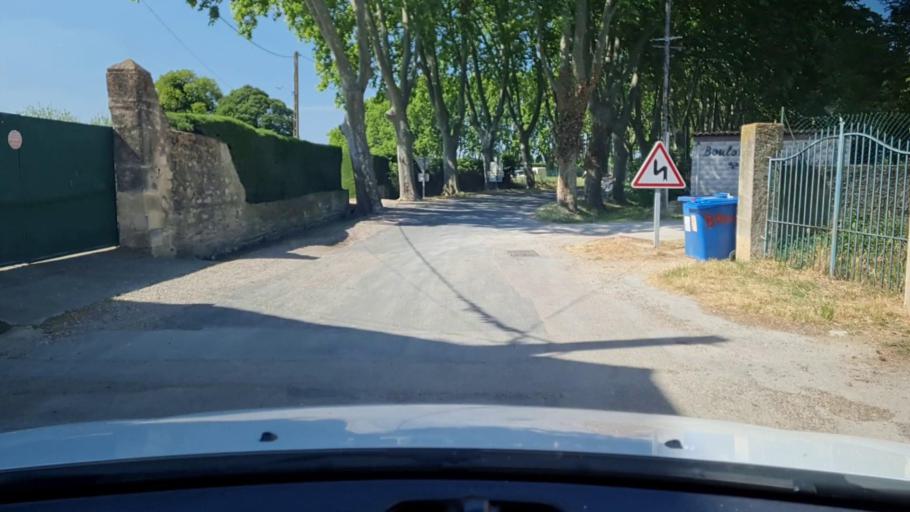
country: FR
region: Languedoc-Roussillon
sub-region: Departement du Gard
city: Le Cailar
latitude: 43.6727
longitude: 4.2366
